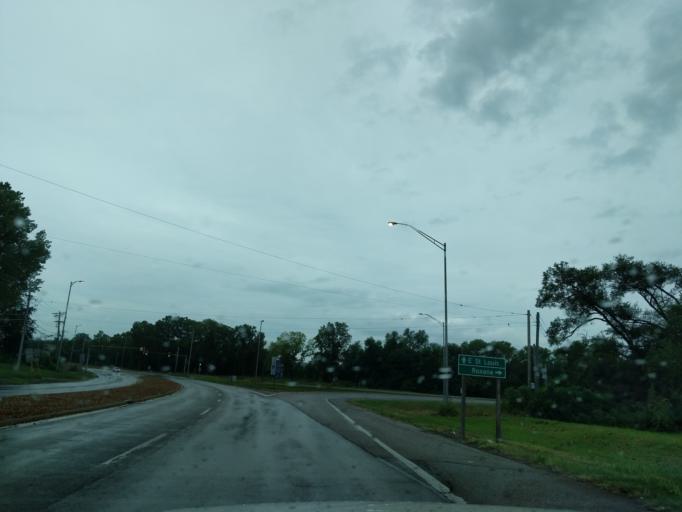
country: US
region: Illinois
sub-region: Saint Clair County
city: Fairmont City
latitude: 38.6594
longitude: -90.0923
